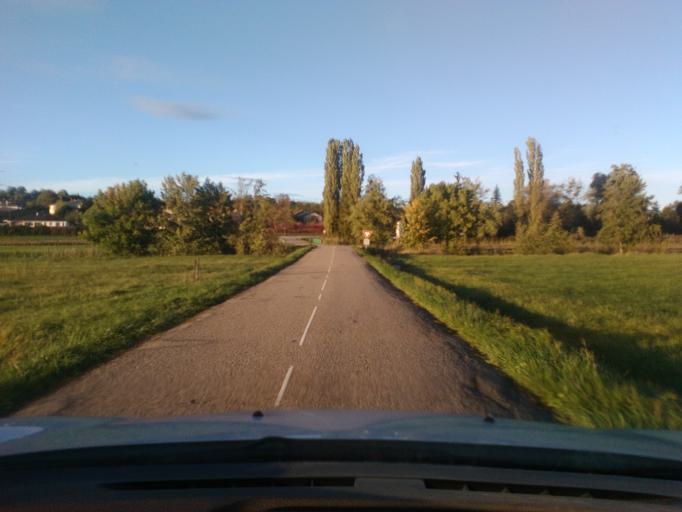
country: FR
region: Lorraine
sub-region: Departement des Vosges
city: Charmes
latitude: 48.3603
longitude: 6.2569
